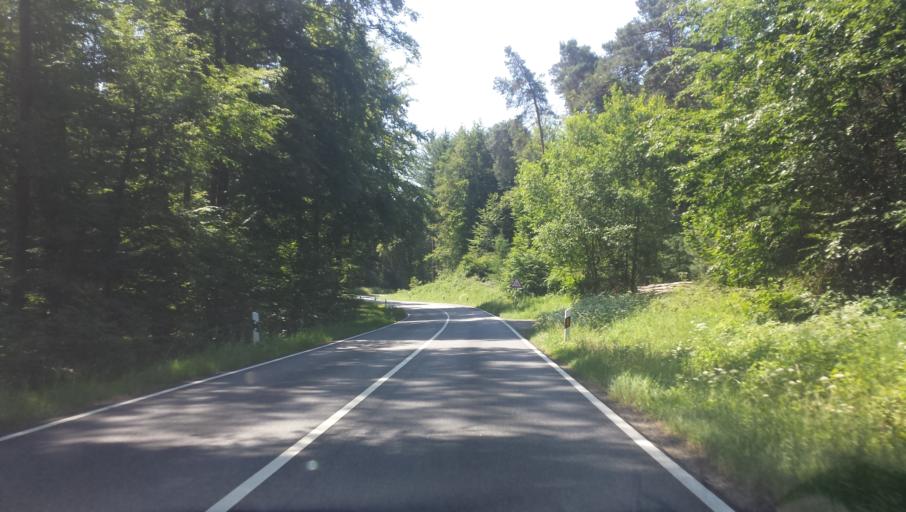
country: DE
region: Rheinland-Pfalz
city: Waldleiningen
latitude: 49.4249
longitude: 7.8876
